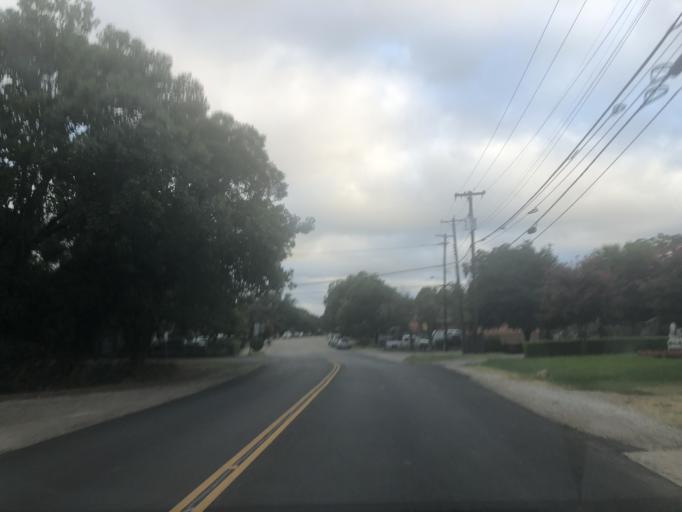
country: US
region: Texas
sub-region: Dallas County
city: University Park
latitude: 32.8311
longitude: -96.8478
